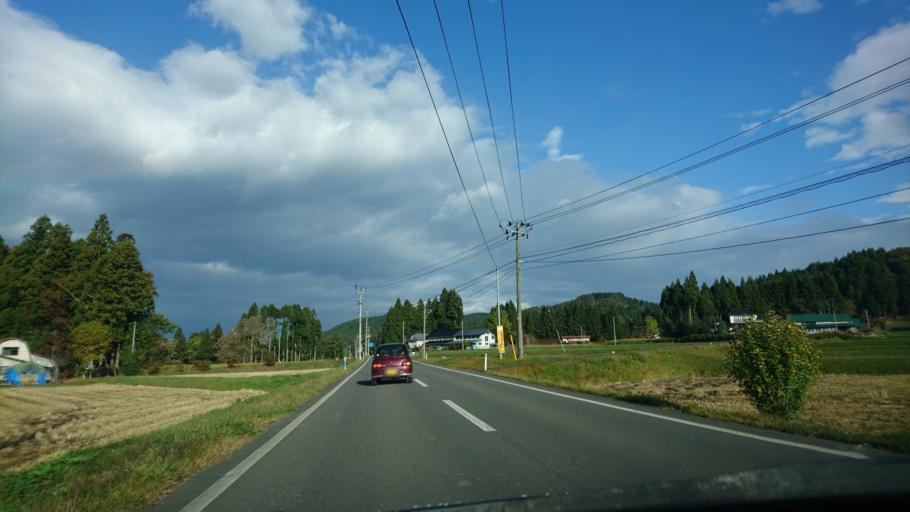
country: JP
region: Iwate
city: Mizusawa
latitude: 39.0515
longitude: 141.0460
